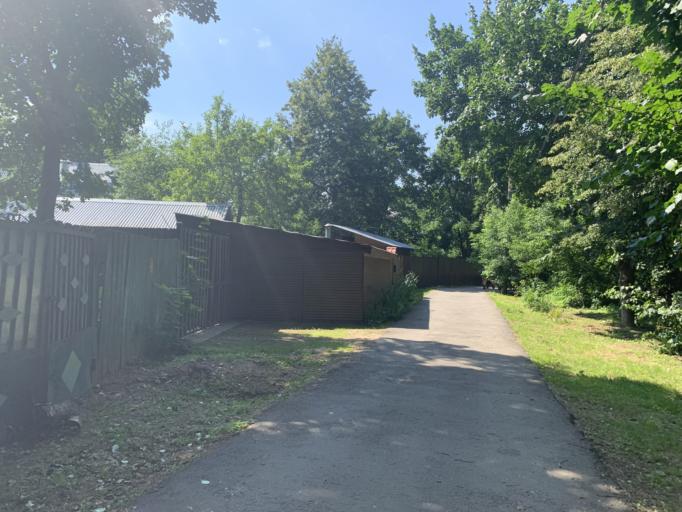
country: RU
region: Moskovskaya
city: Mamontovka
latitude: 55.9692
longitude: 37.8087
